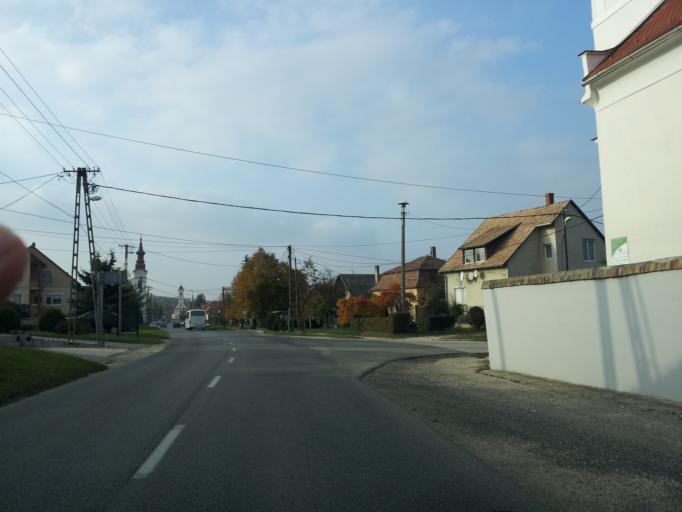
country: HU
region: Komarom-Esztergom
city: Bokod
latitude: 47.4916
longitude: 18.2487
